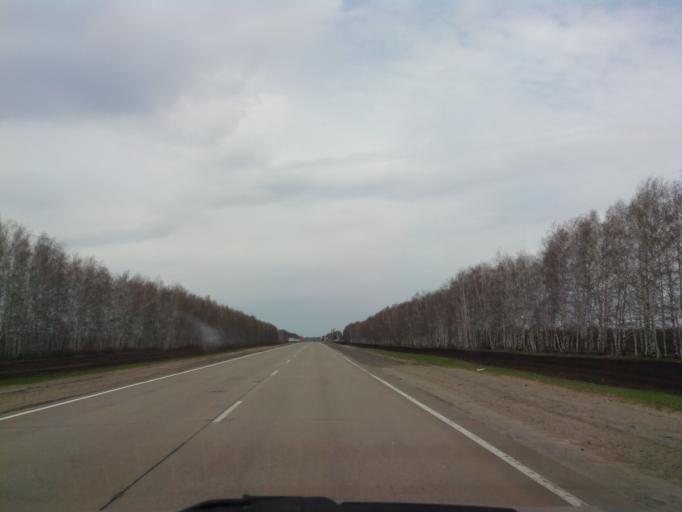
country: RU
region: Tambov
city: Satinka
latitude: 52.2203
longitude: 41.5516
